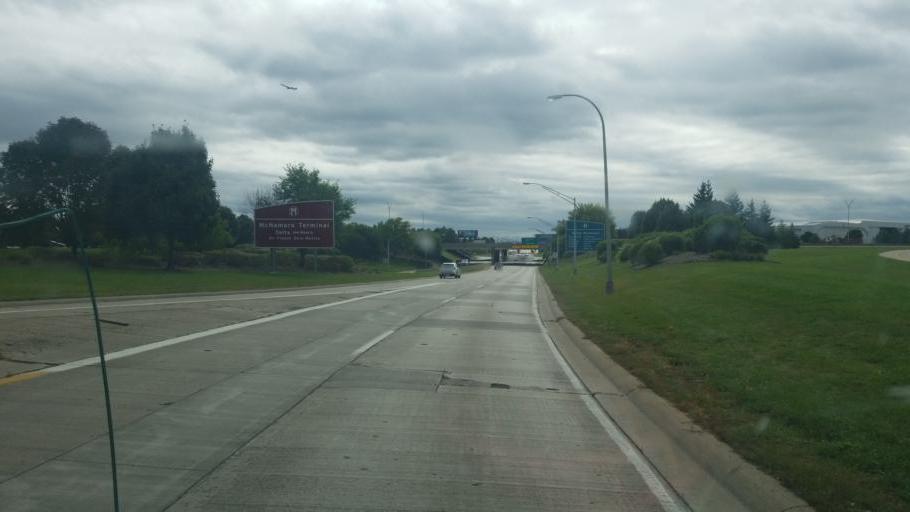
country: US
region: Michigan
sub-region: Wayne County
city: Romulus
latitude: 42.2412
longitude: -83.3428
